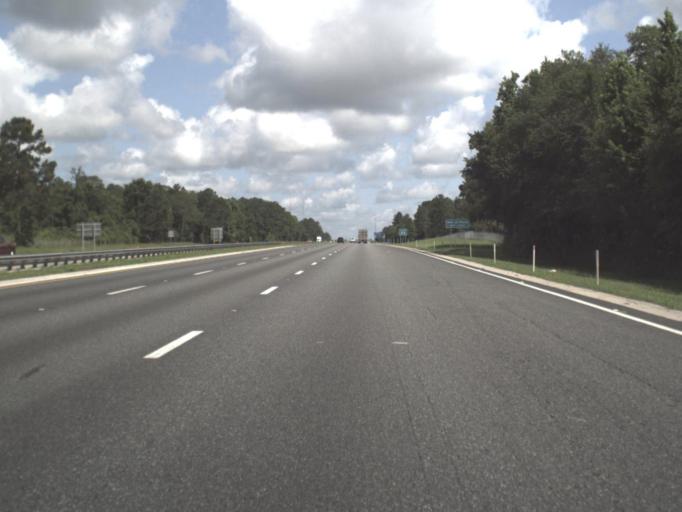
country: US
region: Florida
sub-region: Alachua County
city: Gainesville
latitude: 29.5944
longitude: -82.3662
